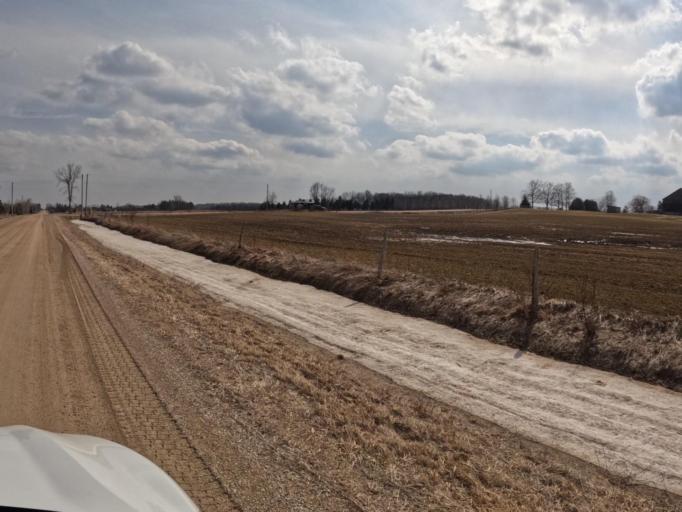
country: CA
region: Ontario
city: Shelburne
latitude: 43.9514
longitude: -80.3133
